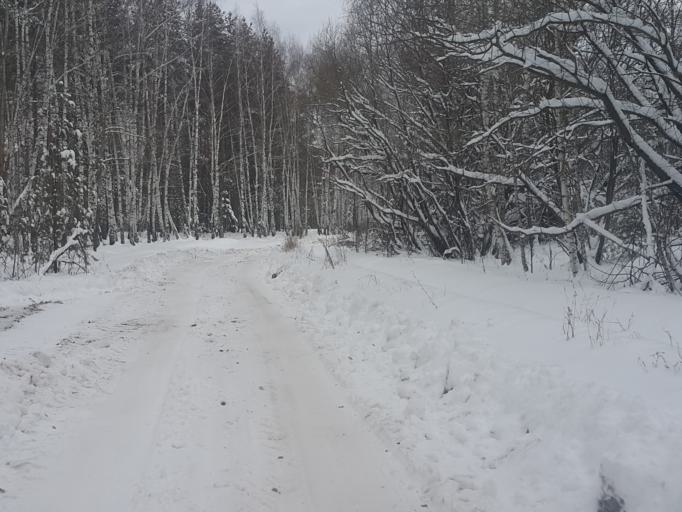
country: RU
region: Tambov
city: Platonovka
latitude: 52.8918
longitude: 41.8471
